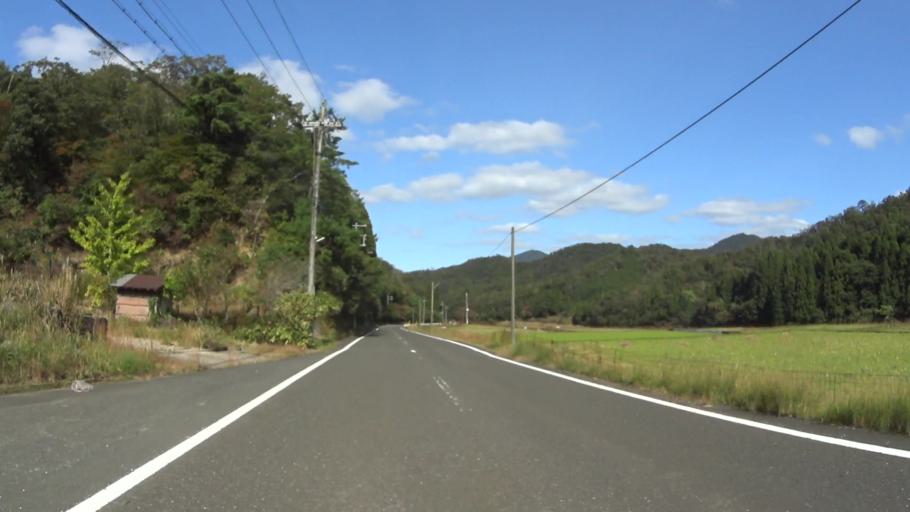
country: JP
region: Hyogo
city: Toyooka
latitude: 35.5539
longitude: 134.9775
